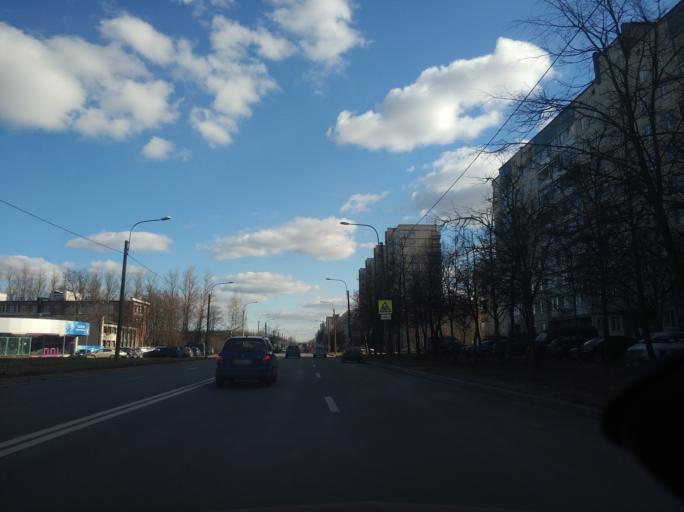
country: RU
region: St.-Petersburg
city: Krasnogvargeisky
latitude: 59.9561
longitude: 30.4947
